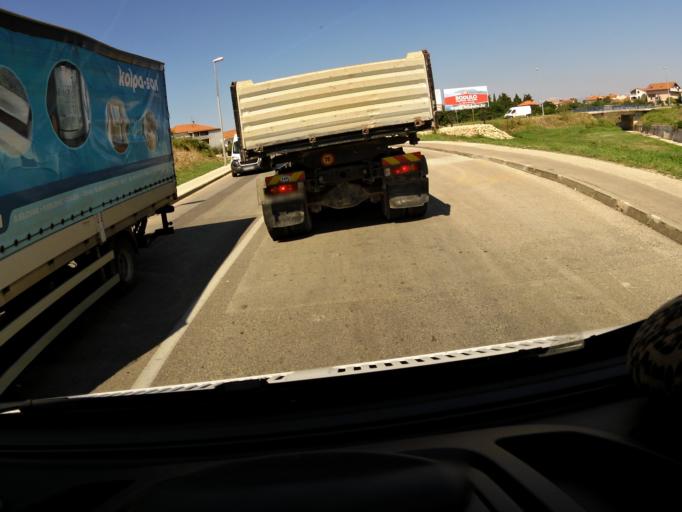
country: HR
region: Zadarska
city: Zadar
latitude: 44.1009
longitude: 15.2558
